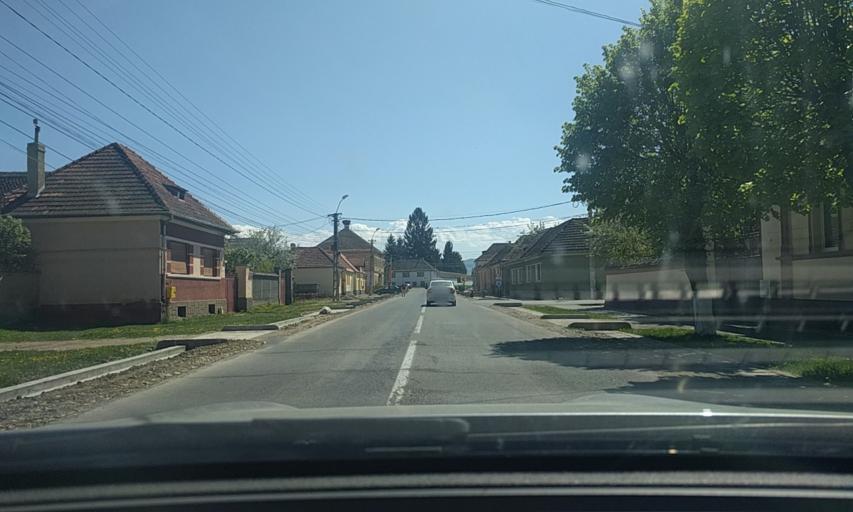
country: RO
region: Brasov
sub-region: Comuna Prejmer
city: Prejmer
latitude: 45.7158
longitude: 25.7782
